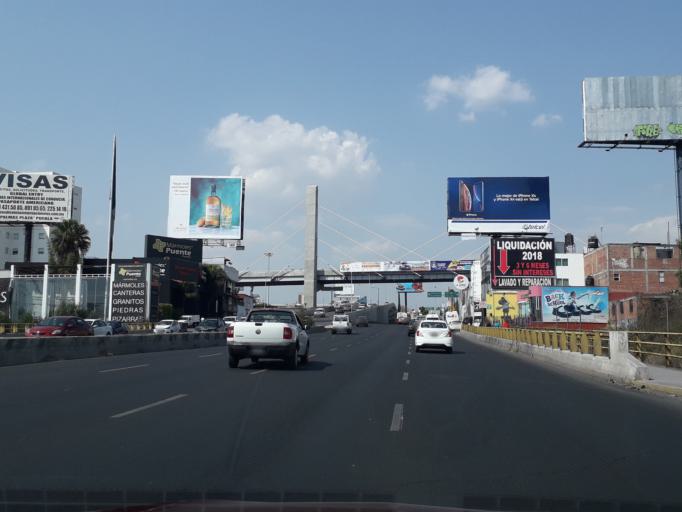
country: MX
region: Puebla
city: Puebla
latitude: 19.0356
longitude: -98.2266
